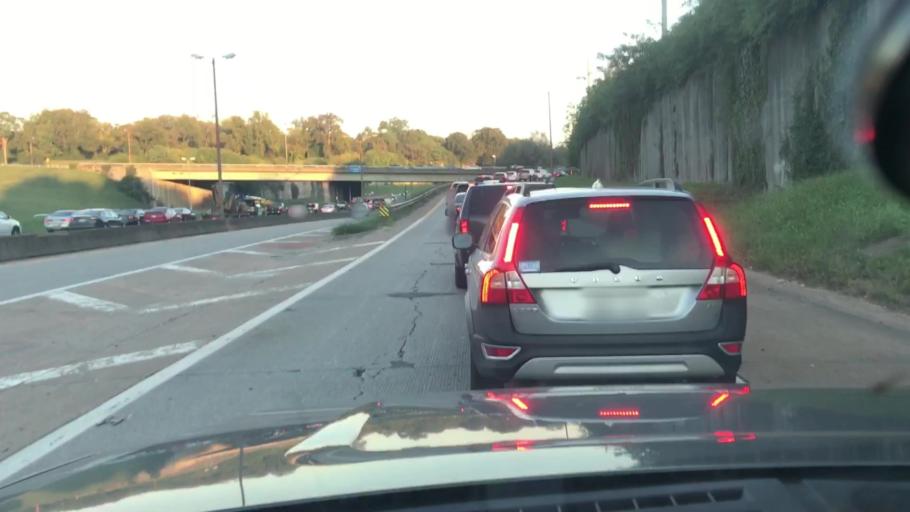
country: US
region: Tennessee
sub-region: Davidson County
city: Oak Hill
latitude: 36.1233
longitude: -86.8091
